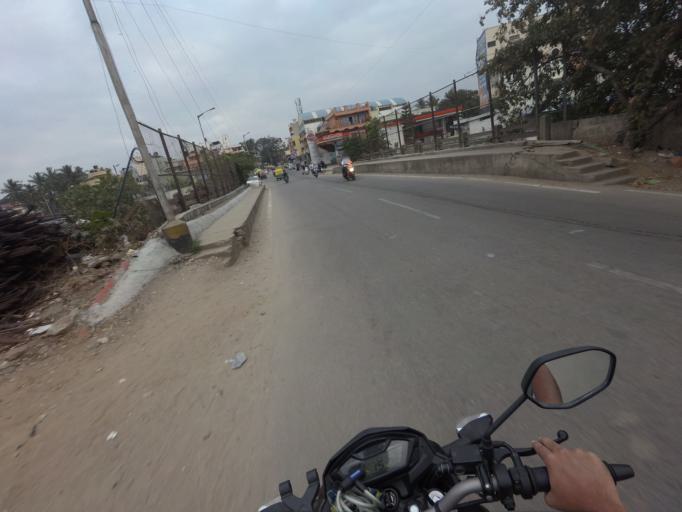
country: IN
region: Karnataka
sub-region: Bangalore Urban
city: Bangalore
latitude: 12.9669
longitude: 77.5466
